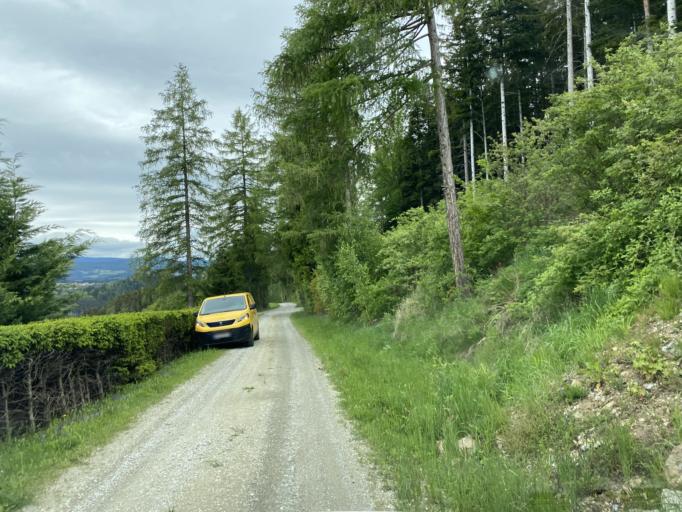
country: AT
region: Styria
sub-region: Politischer Bezirk Weiz
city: Koglhof
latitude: 47.3205
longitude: 15.7014
